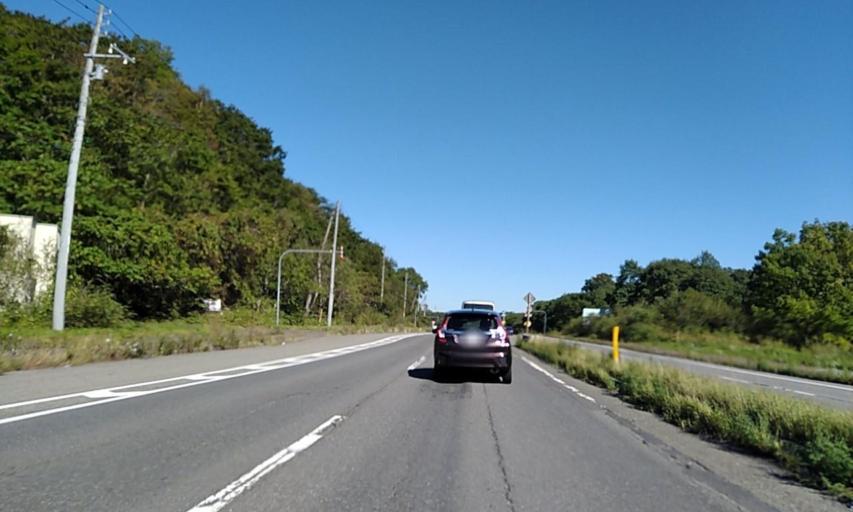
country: JP
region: Hokkaido
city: Chitose
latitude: 42.7570
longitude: 141.7107
